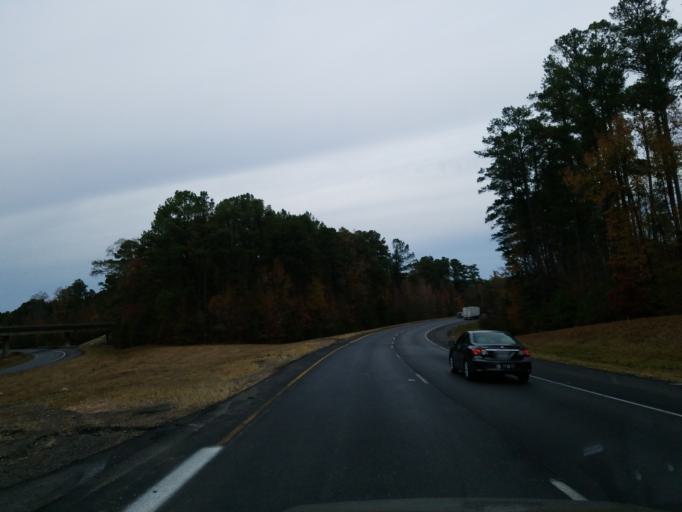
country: US
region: Mississippi
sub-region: Lauderdale County
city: Nellieburg
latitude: 32.3396
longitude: -88.7710
